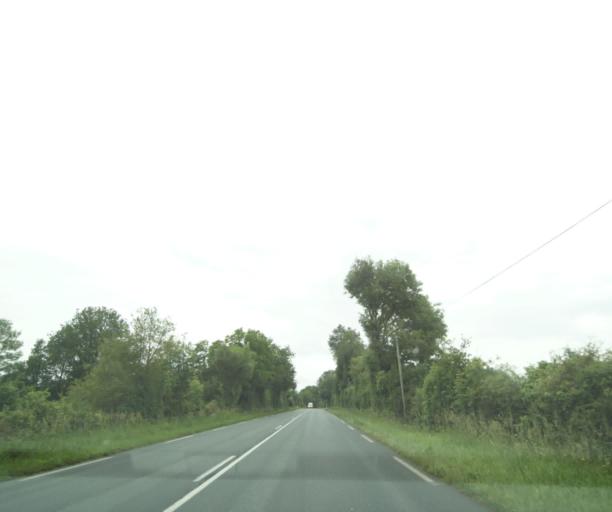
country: FR
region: Poitou-Charentes
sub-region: Departement des Deux-Sevres
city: Viennay
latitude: 46.7083
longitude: -0.2393
